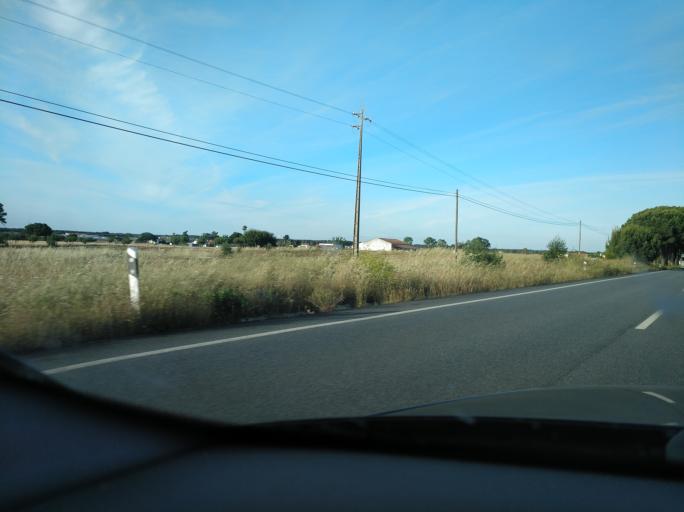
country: PT
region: Santarem
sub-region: Benavente
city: Poceirao
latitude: 38.6829
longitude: -8.6993
